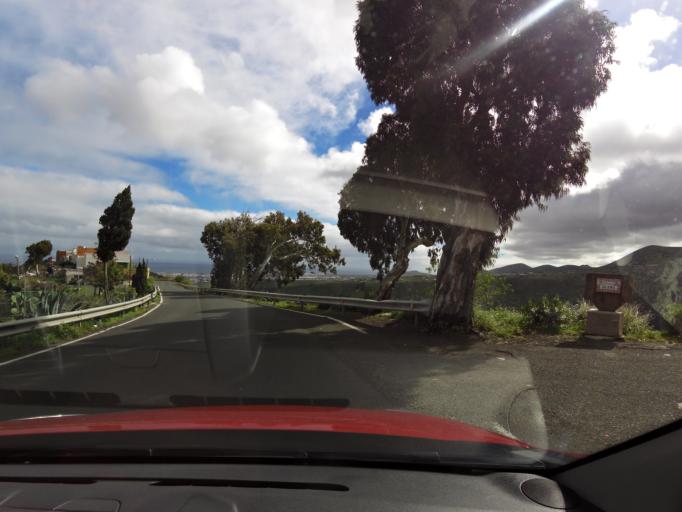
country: ES
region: Canary Islands
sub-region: Provincia de Las Palmas
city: Telde
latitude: 28.0169
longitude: -15.4521
